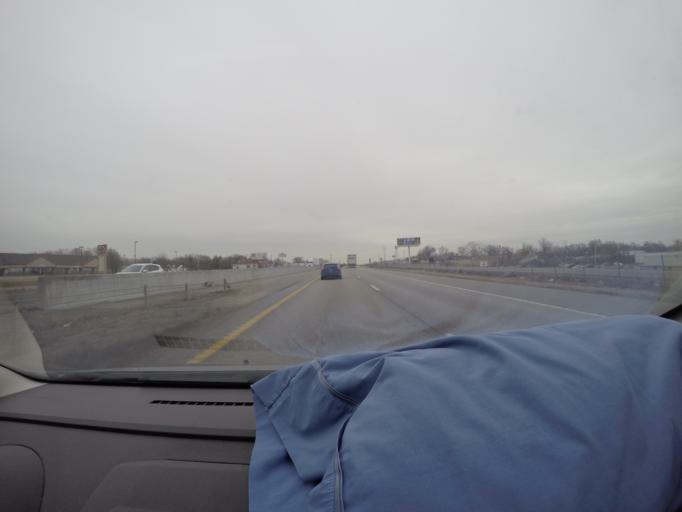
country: US
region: Missouri
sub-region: Warren County
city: Wright City
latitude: 38.8295
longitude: -91.0276
